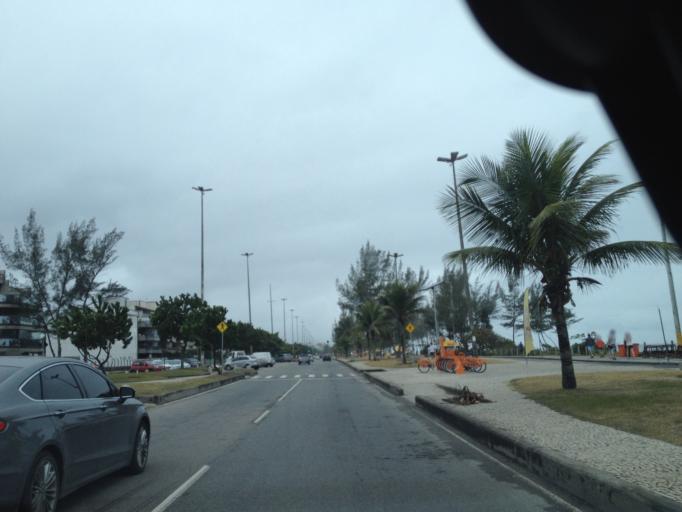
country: BR
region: Rio de Janeiro
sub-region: Nilopolis
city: Nilopolis
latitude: -23.0272
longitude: -43.4637
